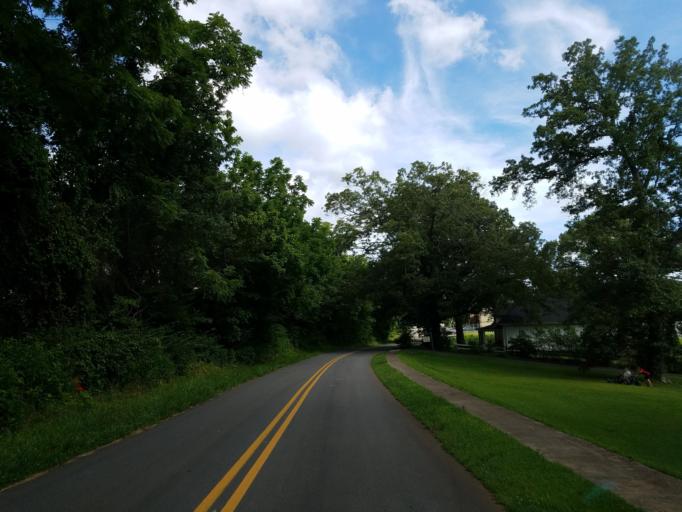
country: US
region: Georgia
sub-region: Pickens County
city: Nelson
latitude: 34.4154
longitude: -84.3879
